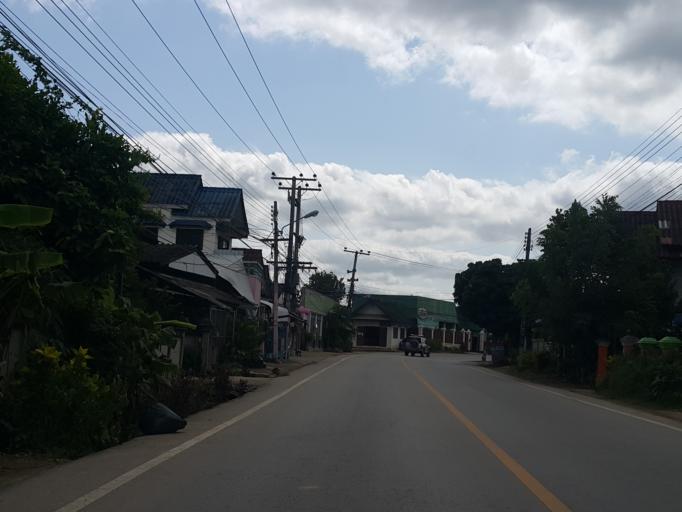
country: TH
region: Lamphun
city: Ban Thi
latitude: 18.6304
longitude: 99.1027
